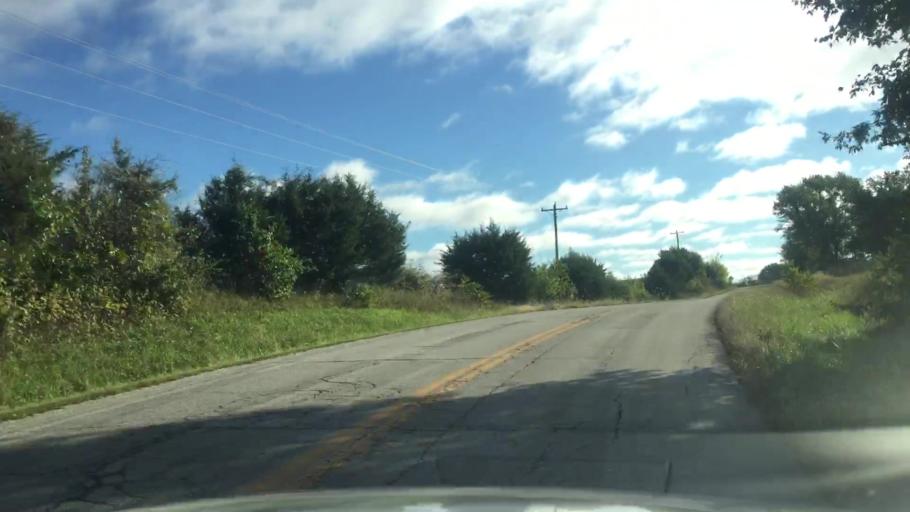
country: US
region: Missouri
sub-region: Howard County
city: New Franklin
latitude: 39.1053
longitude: -92.7691
